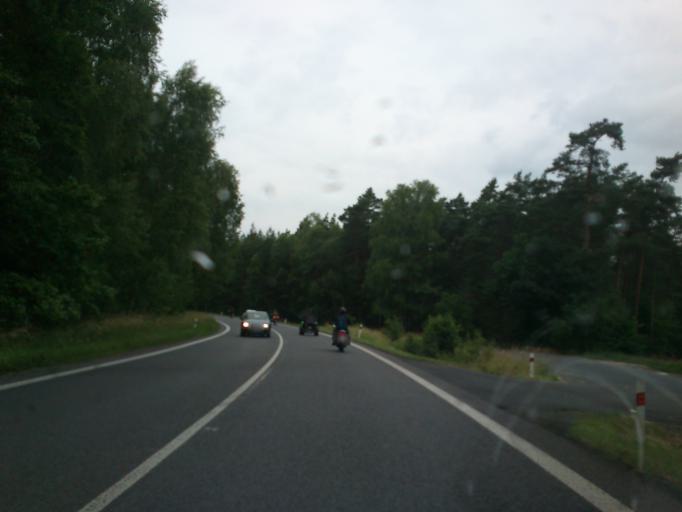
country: CZ
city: Doksy
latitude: 50.5404
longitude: 14.6792
